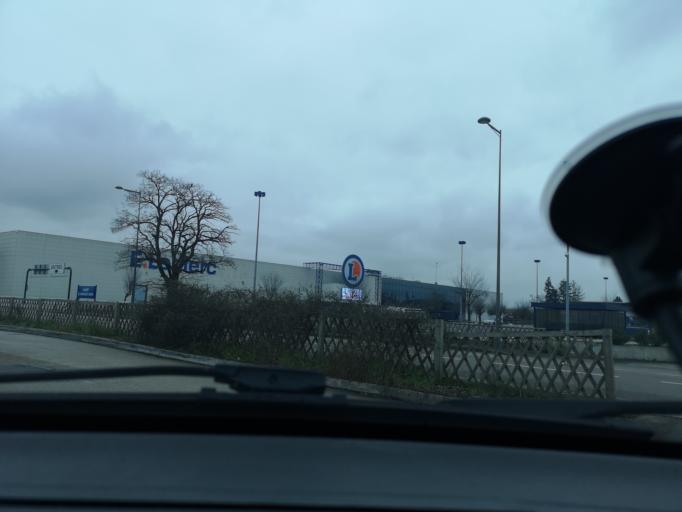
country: FR
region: Bourgogne
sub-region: Departement de Saone-et-Loire
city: Virey-le-Grand
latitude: 46.8132
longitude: 4.8567
